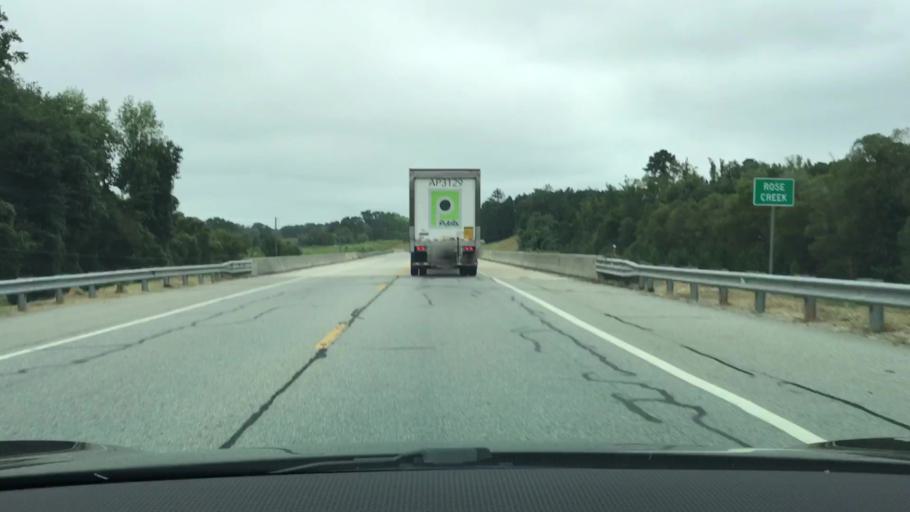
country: US
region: Georgia
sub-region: Oconee County
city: Watkinsville
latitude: 33.7347
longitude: -83.3032
